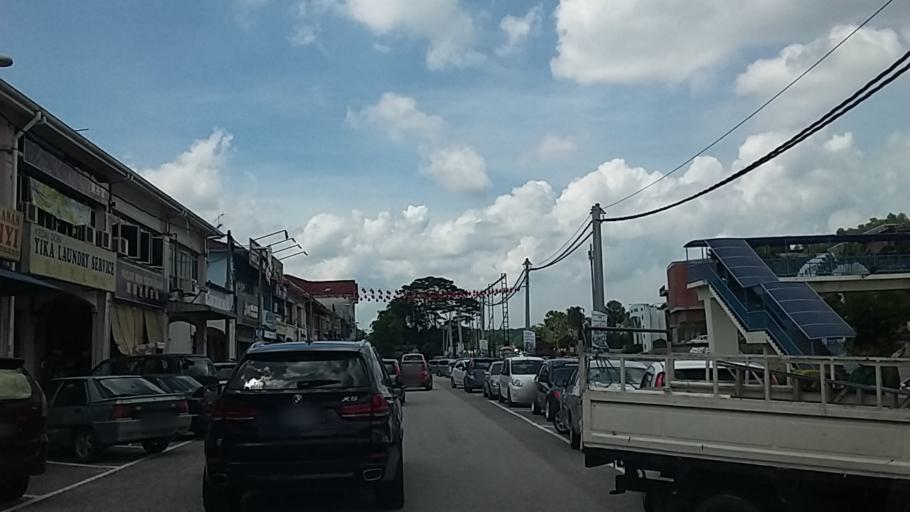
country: MY
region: Johor
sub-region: Daerah Batu Pahat
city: Batu Pahat
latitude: 1.8361
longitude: 102.9482
